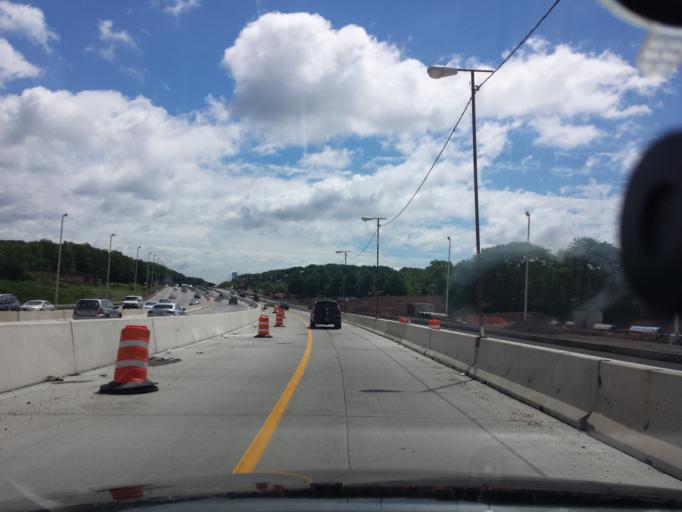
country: US
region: New York
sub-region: Richmond County
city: Staten Island
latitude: 40.6103
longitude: -74.1100
